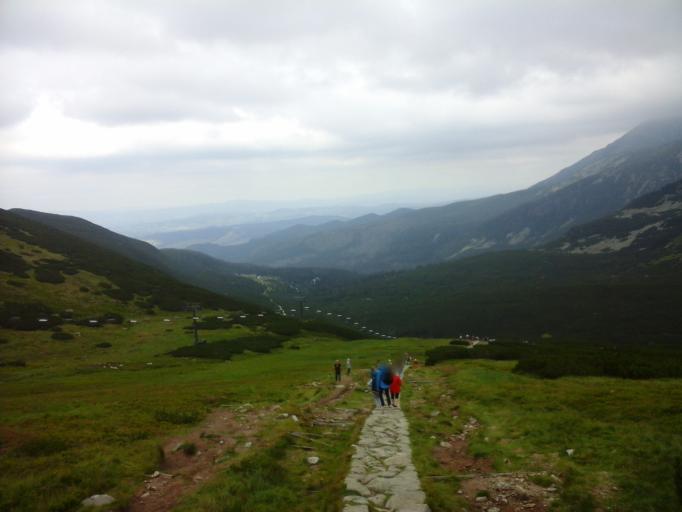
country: PL
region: Lesser Poland Voivodeship
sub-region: Powiat tatrzanski
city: Zakopane
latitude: 49.2335
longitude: 19.9902
